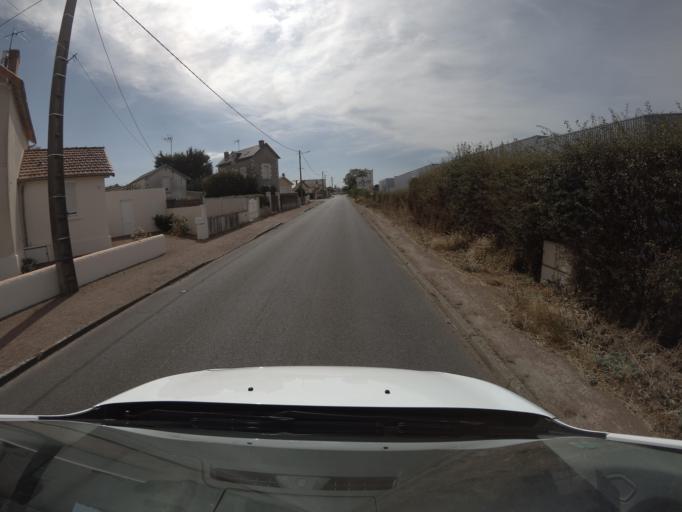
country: FR
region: Poitou-Charentes
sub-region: Departement des Deux-Sevres
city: Thouars
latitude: 46.9796
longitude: -0.1959
